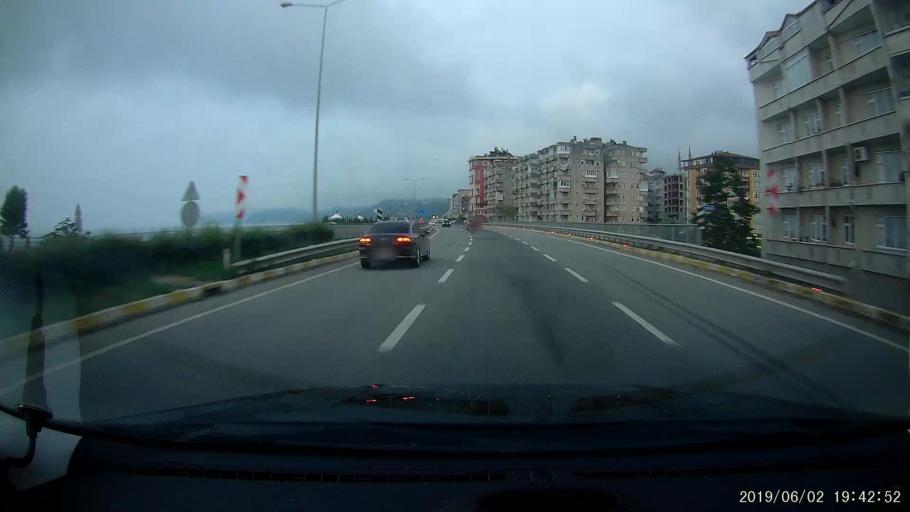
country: TR
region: Giresun
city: Kesap
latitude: 40.9170
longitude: 38.5147
